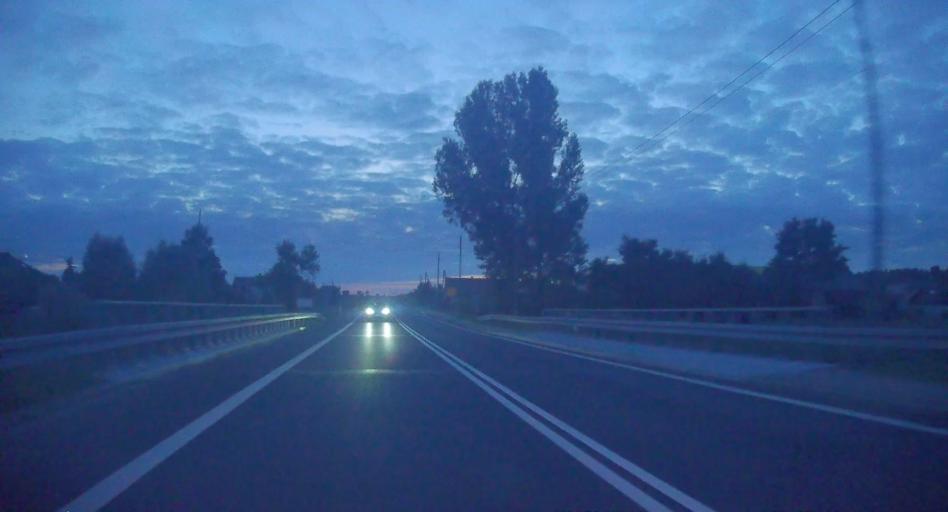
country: PL
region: Silesian Voivodeship
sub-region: Powiat klobucki
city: Lobodno
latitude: 50.8840
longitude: 18.9850
